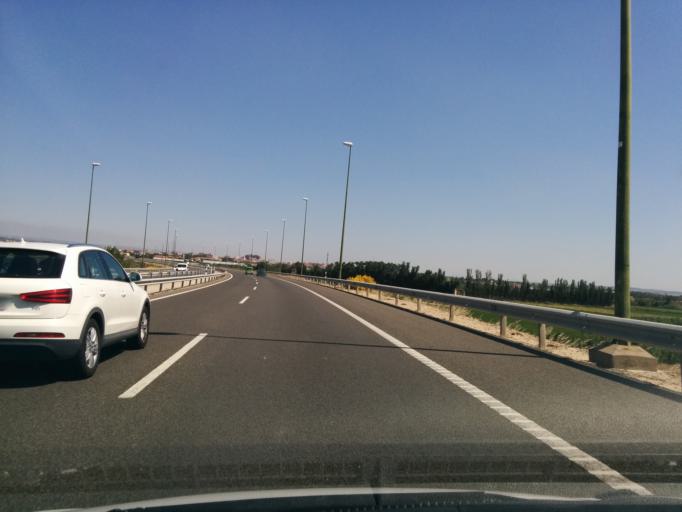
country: ES
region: Aragon
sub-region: Provincia de Zaragoza
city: Zaragoza
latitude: 41.6402
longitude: -0.8312
